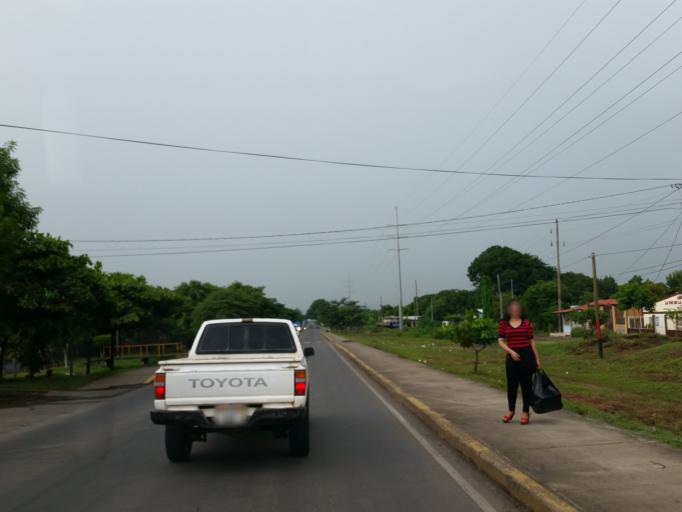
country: NI
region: Chinandega
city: Chinandega
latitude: 12.6532
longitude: -87.1236
